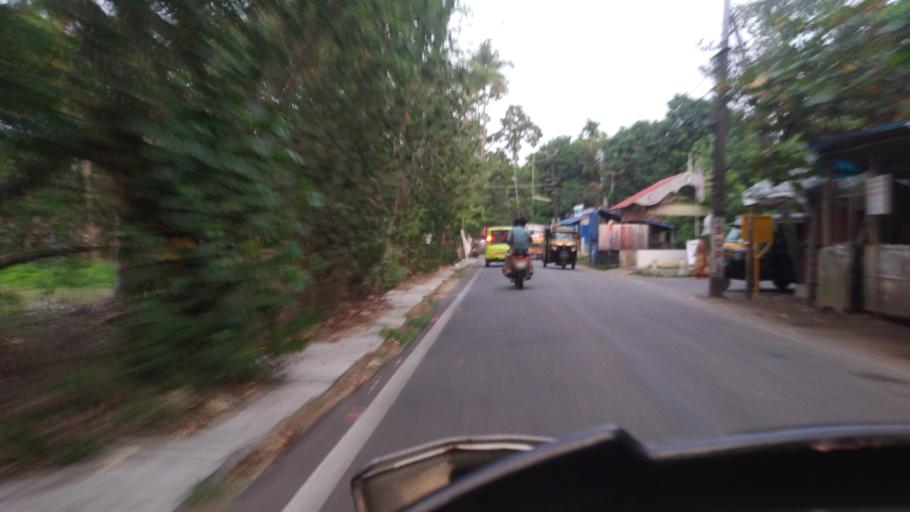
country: IN
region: Kerala
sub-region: Thrissur District
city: Kodungallur
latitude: 10.1655
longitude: 76.2036
